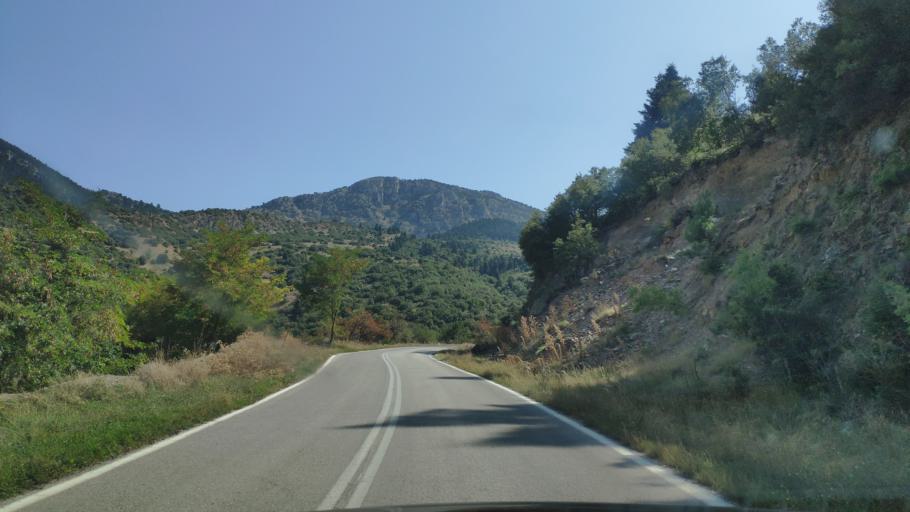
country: GR
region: West Greece
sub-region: Nomos Achaias
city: Aiyira
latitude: 37.9212
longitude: 22.3353
